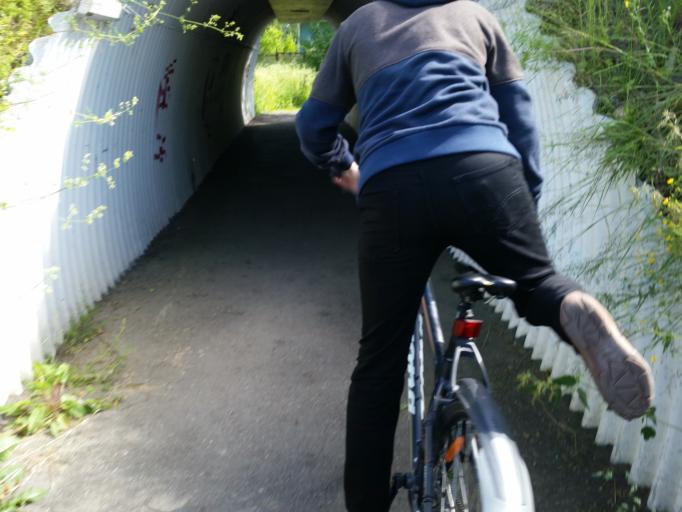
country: FI
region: Northern Savo
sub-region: Varkaus
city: Varkaus
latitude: 62.3379
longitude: 27.9027
